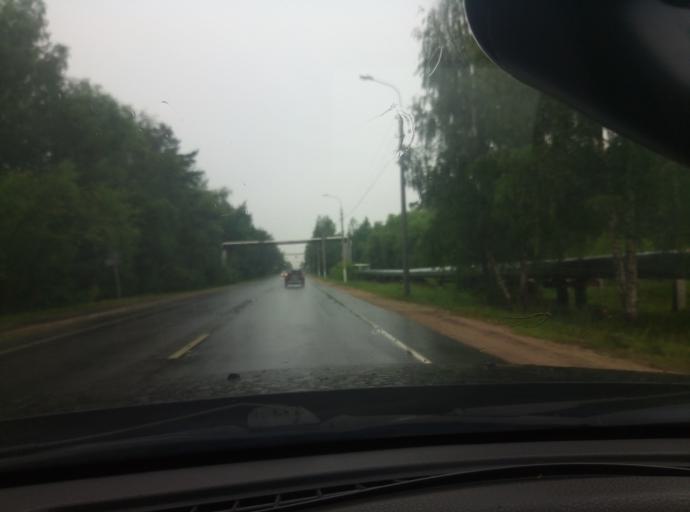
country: RU
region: Moskovskaya
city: Protvino
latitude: 54.8822
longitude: 37.2210
